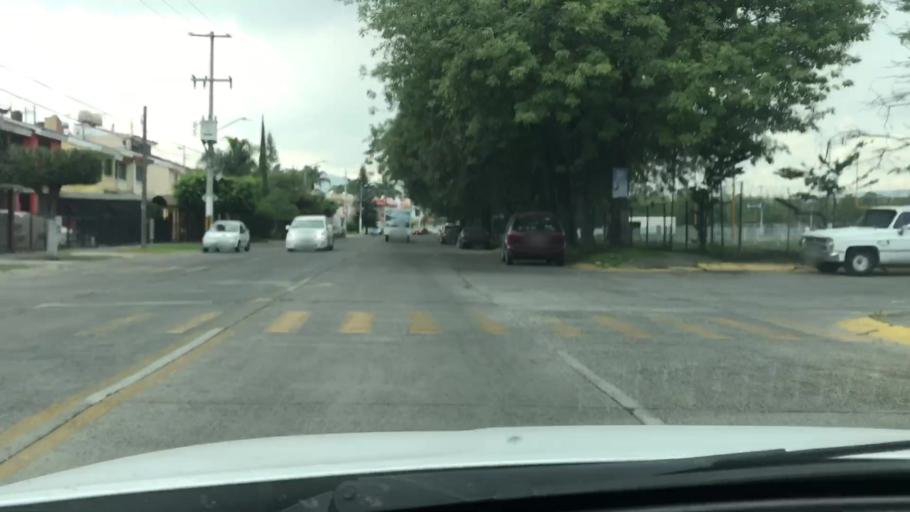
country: MX
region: Jalisco
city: Guadalajara
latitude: 20.6348
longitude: -103.4306
